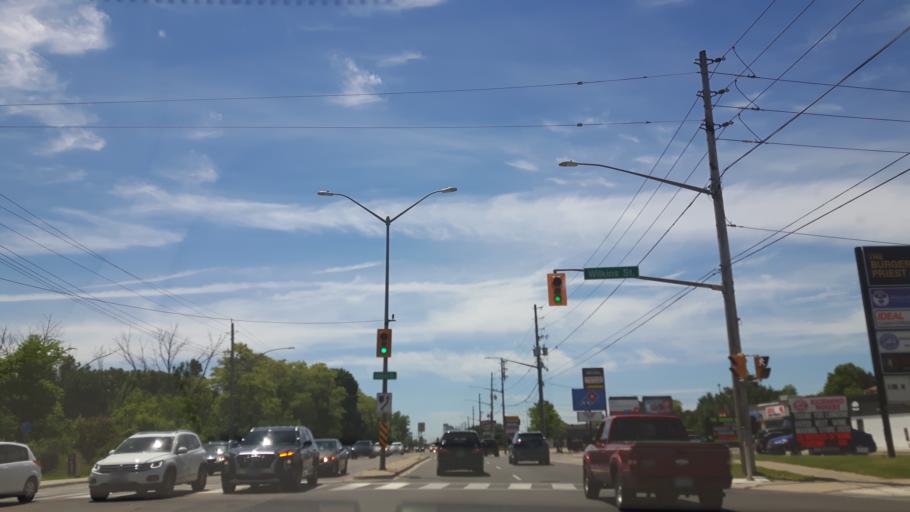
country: CA
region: Ontario
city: London
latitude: 42.9515
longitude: -81.2287
